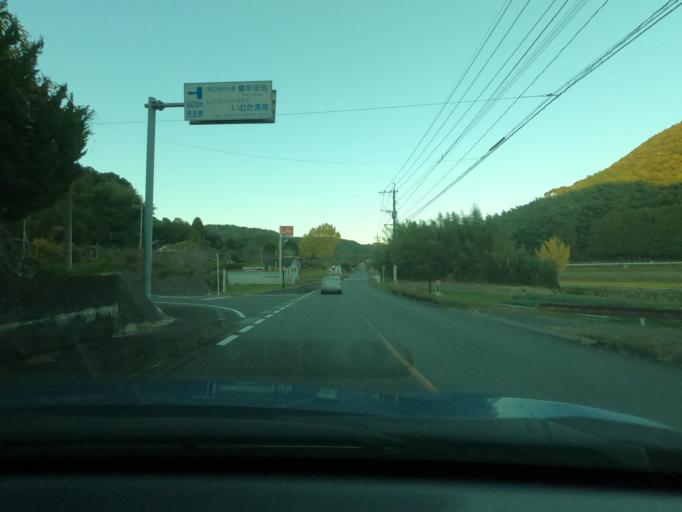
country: JP
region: Kagoshima
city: Satsumasendai
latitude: 31.8043
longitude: 130.4811
